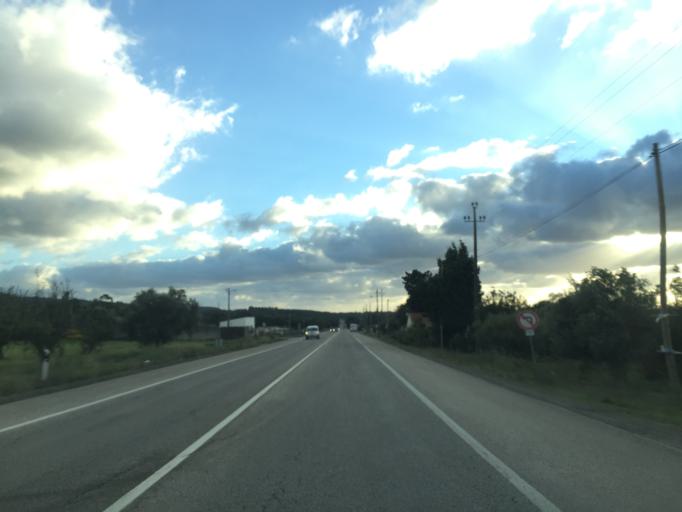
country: PT
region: Leiria
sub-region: Alcobaca
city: Aljubarrota
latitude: 39.5231
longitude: -8.9125
